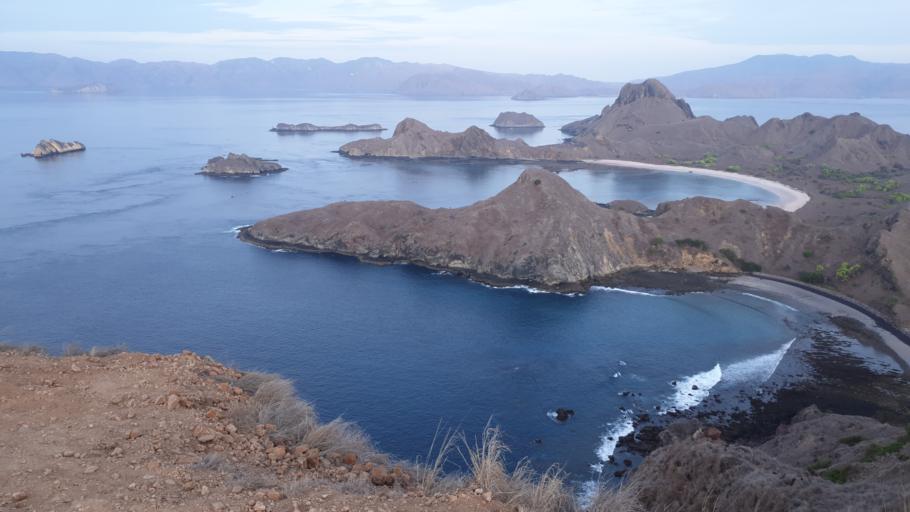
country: ID
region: East Nusa Tenggara
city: Komodo
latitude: -8.6825
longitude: 119.5573
